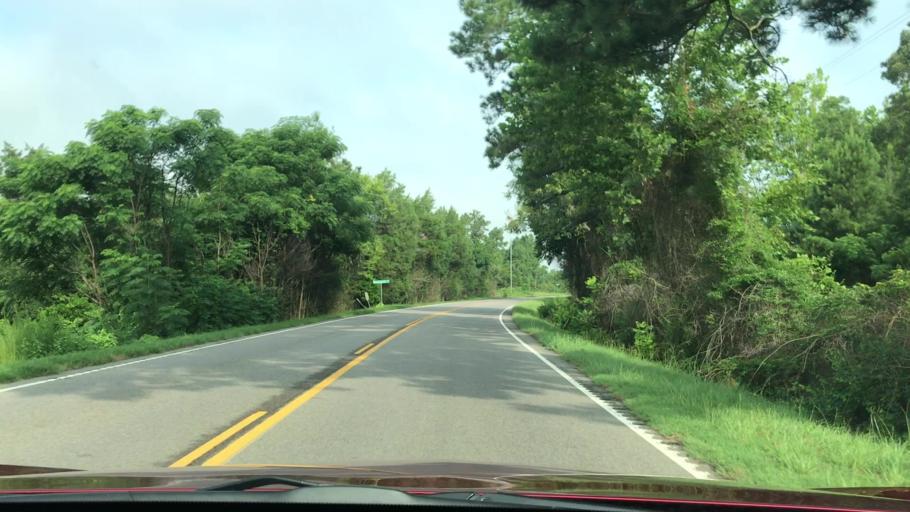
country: US
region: South Carolina
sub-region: Lexington County
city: Batesburg-Leesville
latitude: 33.6901
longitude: -81.4700
